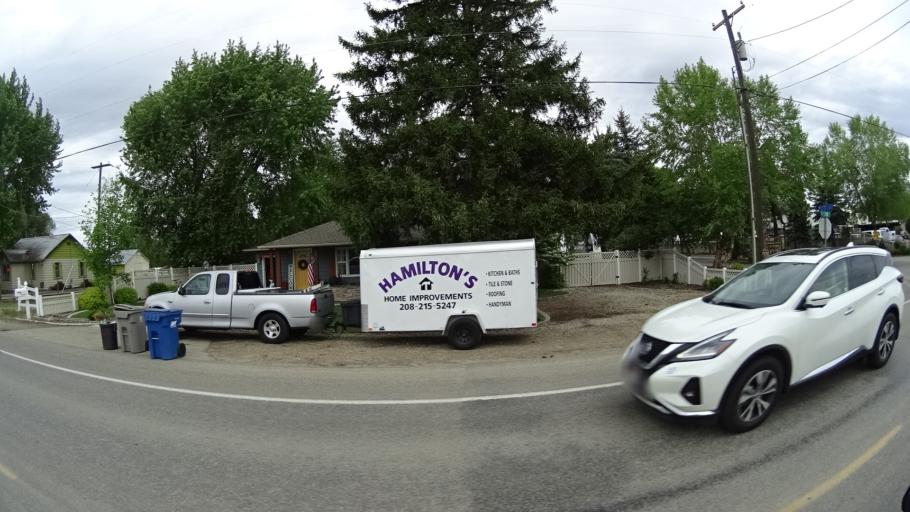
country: US
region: Idaho
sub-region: Ada County
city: Star
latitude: 43.6893
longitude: -116.4932
